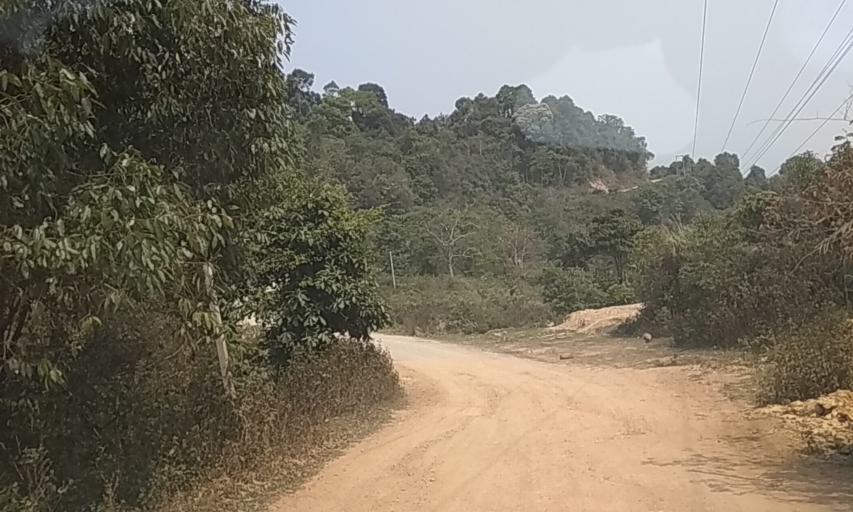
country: TH
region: Nan
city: Chaloem Phra Kiat
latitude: 20.0123
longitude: 101.1160
